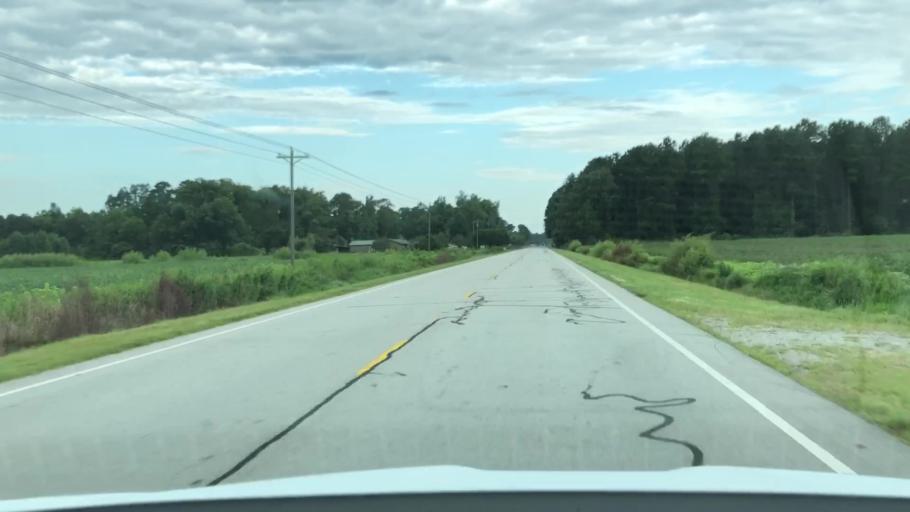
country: US
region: North Carolina
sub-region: Jones County
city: Trenton
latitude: 35.0821
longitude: -77.4375
